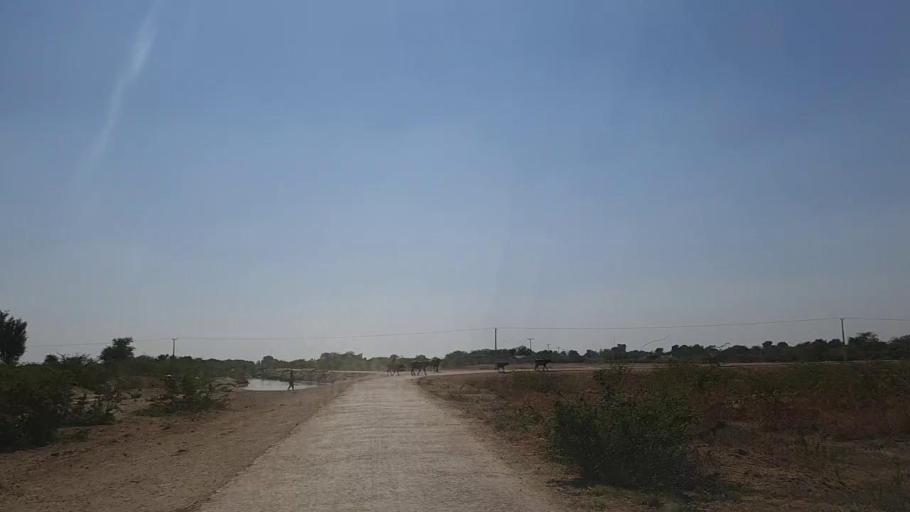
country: PK
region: Sindh
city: Samaro
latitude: 25.3956
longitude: 69.3877
